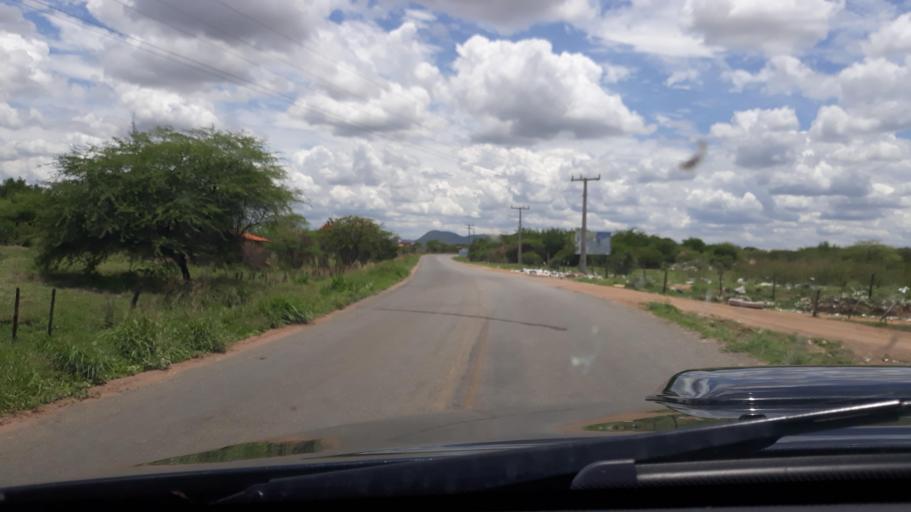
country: BR
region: Bahia
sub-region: Guanambi
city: Guanambi
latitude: -14.1925
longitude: -42.7983
